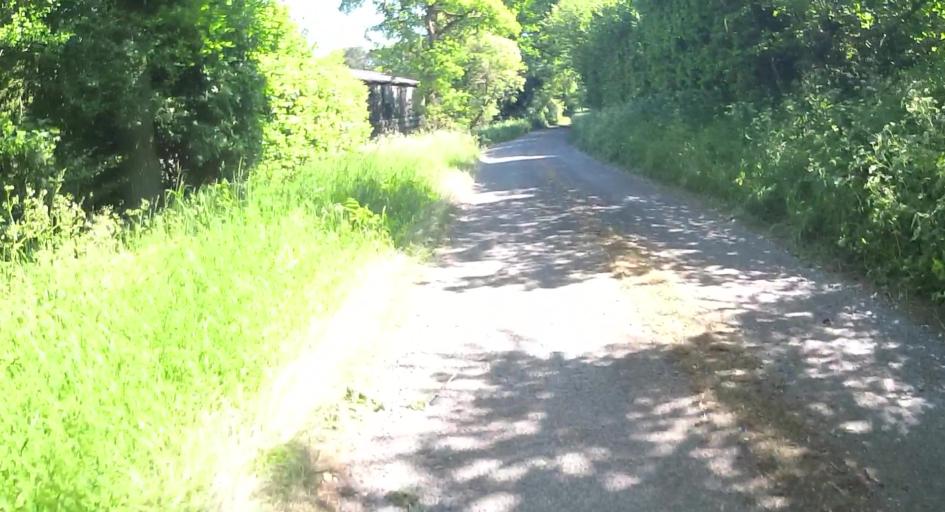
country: GB
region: England
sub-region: Hampshire
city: Overton
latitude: 51.2879
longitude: -1.3088
